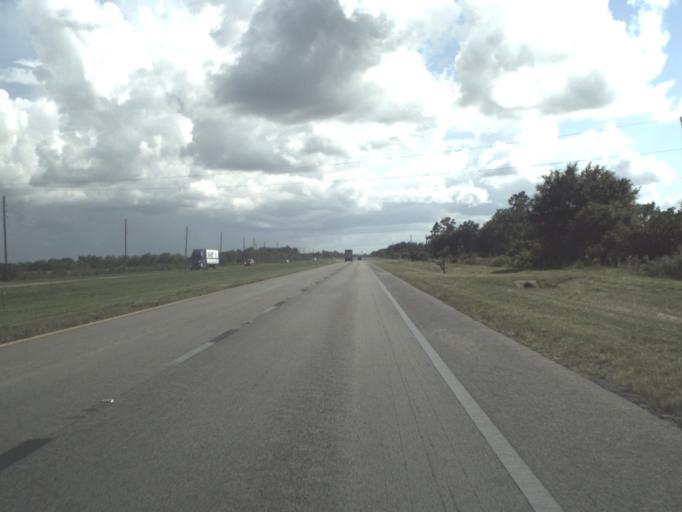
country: US
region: Florida
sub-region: Charlotte County
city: Harbour Heights
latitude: 27.0215
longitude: -81.9587
